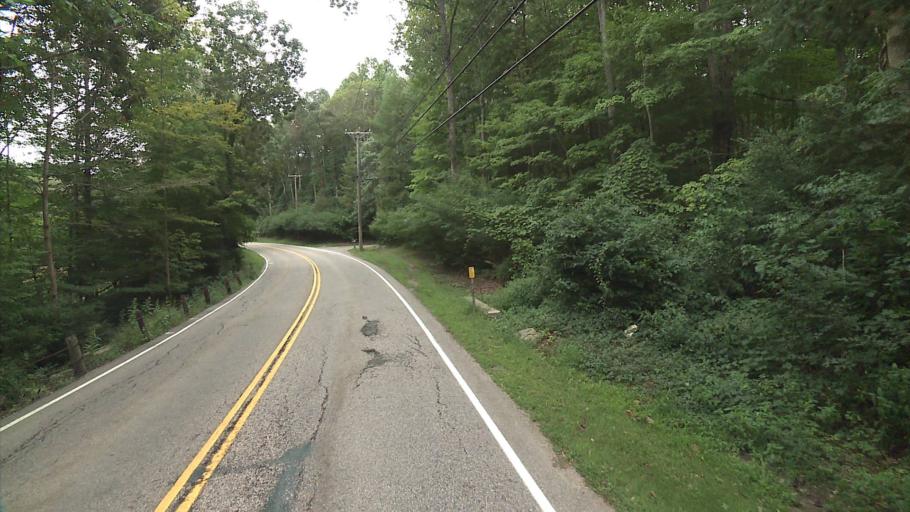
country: US
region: Connecticut
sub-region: Middlesex County
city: Essex Village
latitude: 41.4037
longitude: -72.3412
